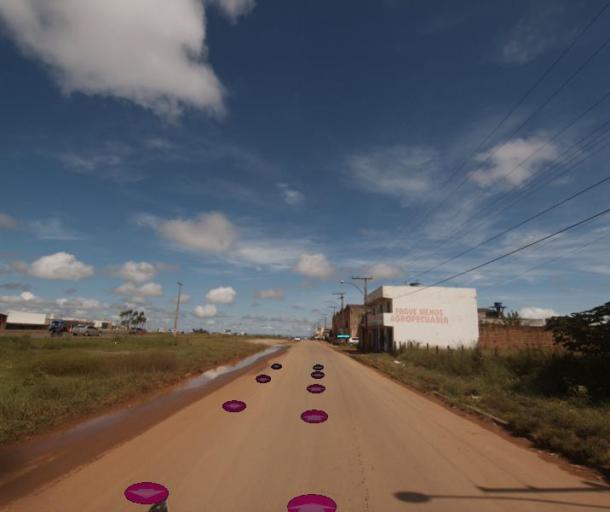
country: BR
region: Federal District
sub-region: Brasilia
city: Brasilia
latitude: -15.7364
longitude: -48.2887
